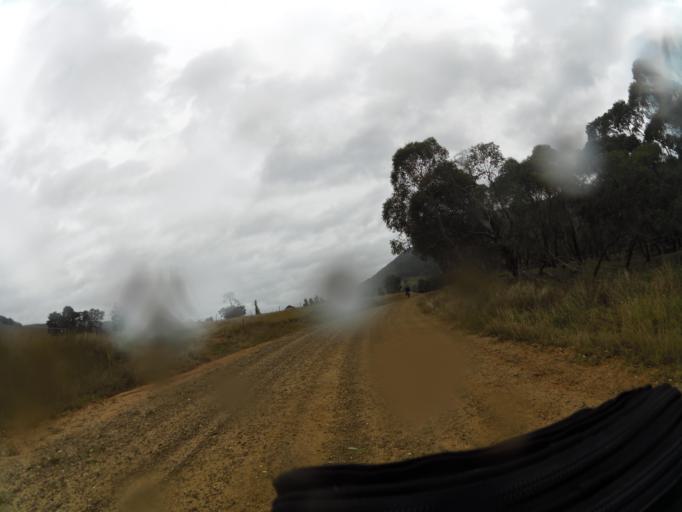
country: AU
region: New South Wales
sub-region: Greater Hume Shire
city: Holbrook
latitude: -36.2393
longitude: 147.6345
